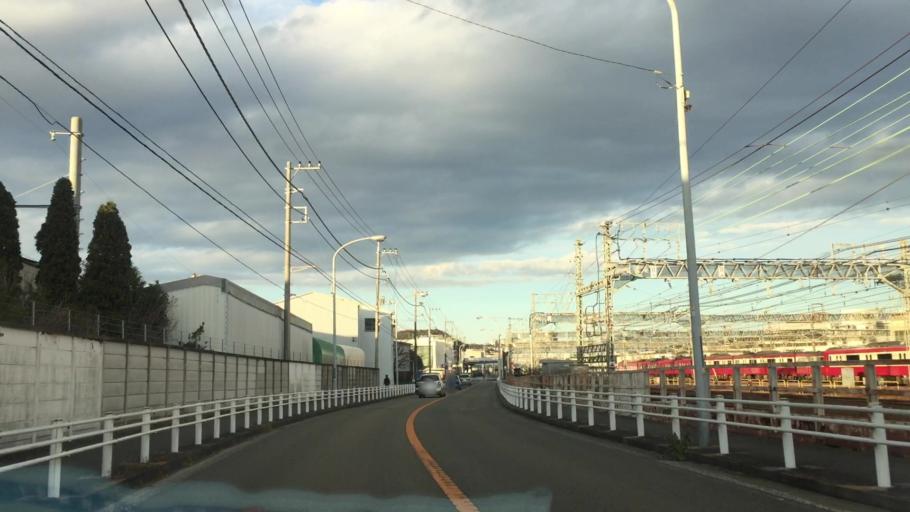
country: JP
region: Kanagawa
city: Zushi
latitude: 35.3367
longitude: 139.6199
